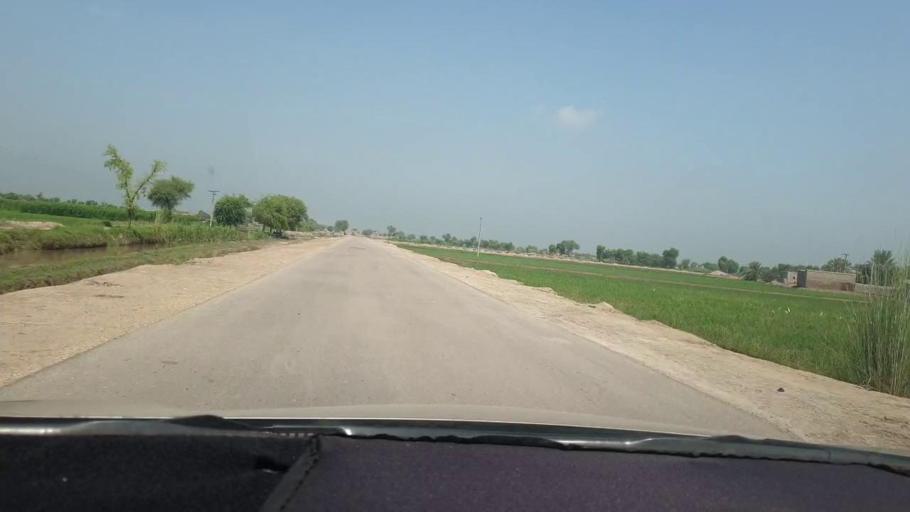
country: PK
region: Sindh
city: Miro Khan
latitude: 27.7795
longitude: 68.0548
